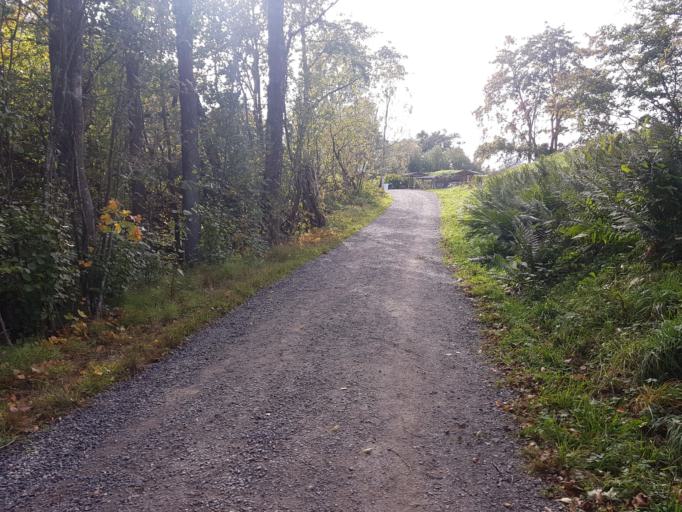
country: FI
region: Uusimaa
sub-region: Helsinki
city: Helsinki
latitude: 60.1382
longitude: 24.9962
